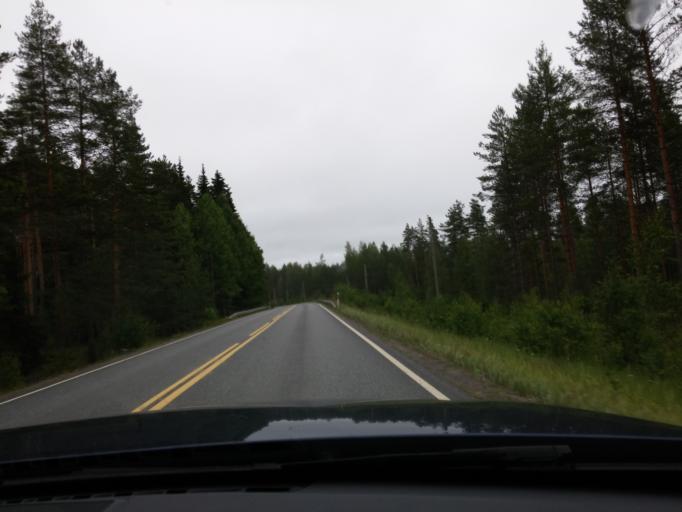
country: FI
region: Central Finland
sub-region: Joutsa
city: Joutsa
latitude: 61.7895
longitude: 26.0195
